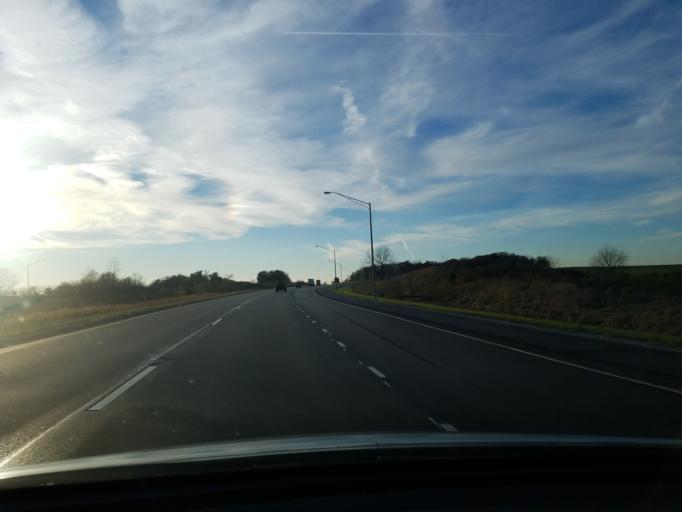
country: US
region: Indiana
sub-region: Spencer County
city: Dale
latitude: 38.1965
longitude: -86.9416
